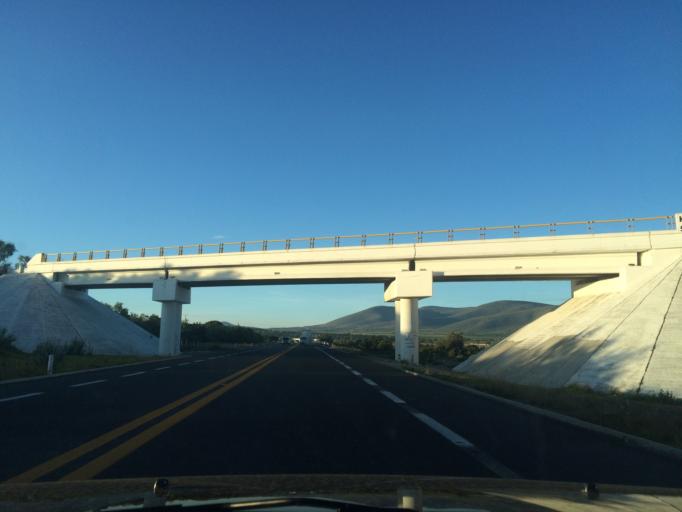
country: MX
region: Puebla
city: Cuacnopalan
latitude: 18.7817
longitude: -97.4878
